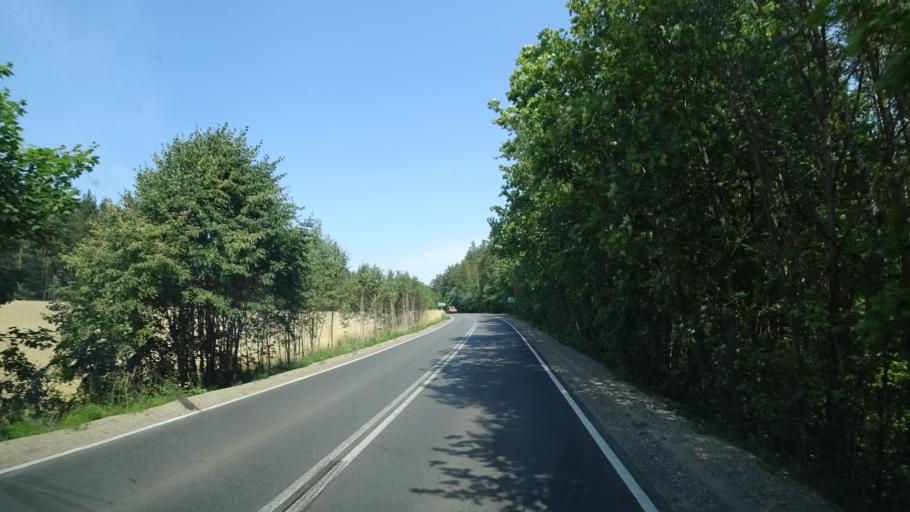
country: PL
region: Pomeranian Voivodeship
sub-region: Powiat koscierski
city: Dziemiany
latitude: 53.9791
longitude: 17.7730
